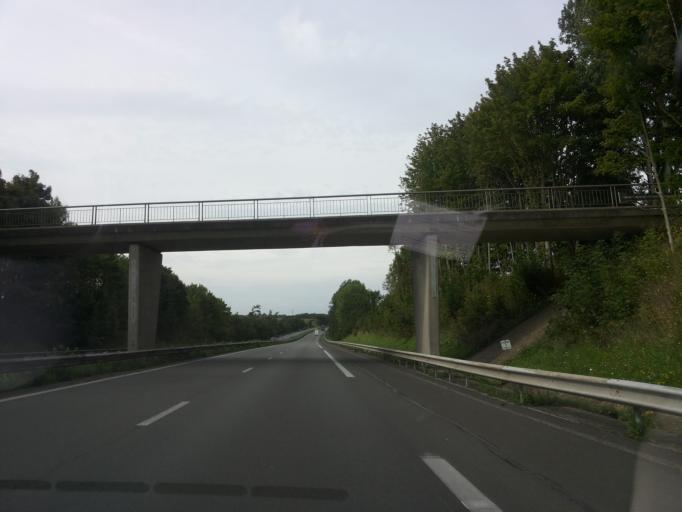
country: FR
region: Nord-Pas-de-Calais
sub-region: Departement du Pas-de-Calais
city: Norrent-Fontes
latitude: 50.5591
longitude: 2.4243
